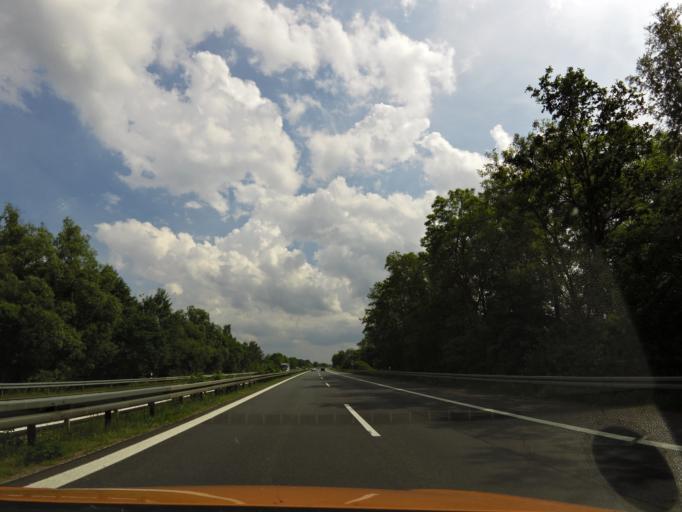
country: DE
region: Brandenburg
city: Gerdshagen
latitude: 53.2028
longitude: 12.2664
